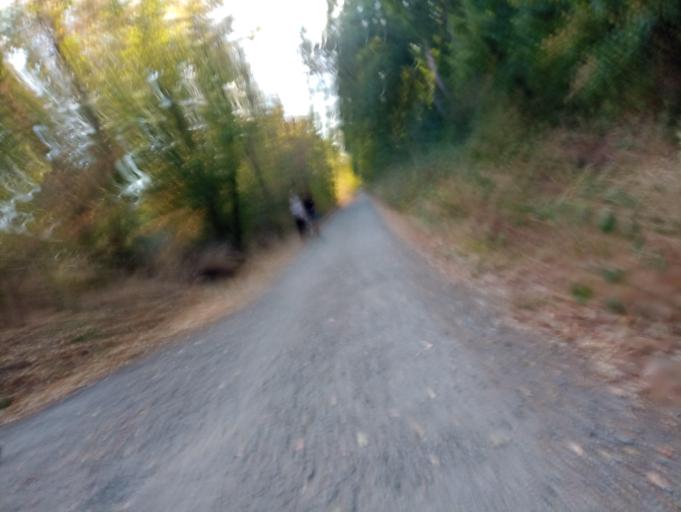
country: DE
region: Hesse
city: Niederrad
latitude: 50.0691
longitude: 8.6337
